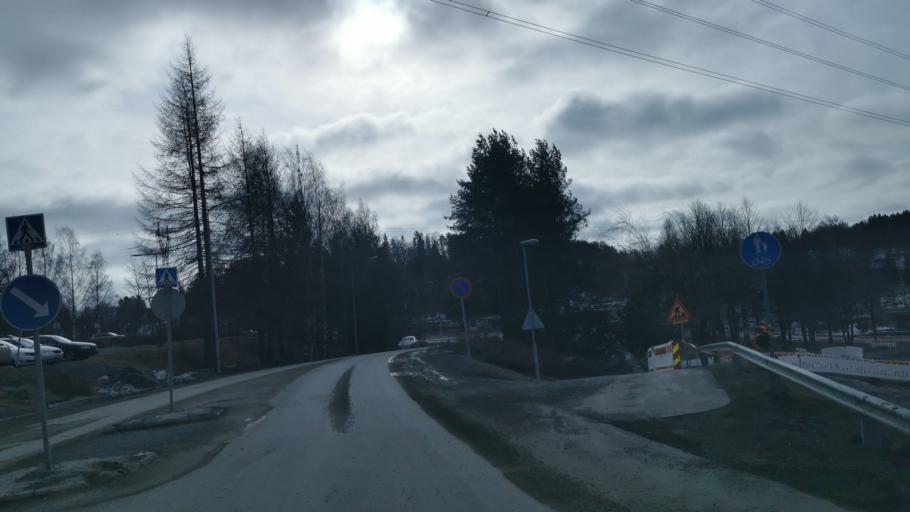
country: FI
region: Northern Savo
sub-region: Kuopio
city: Kuopio
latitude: 62.8960
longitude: 27.6445
